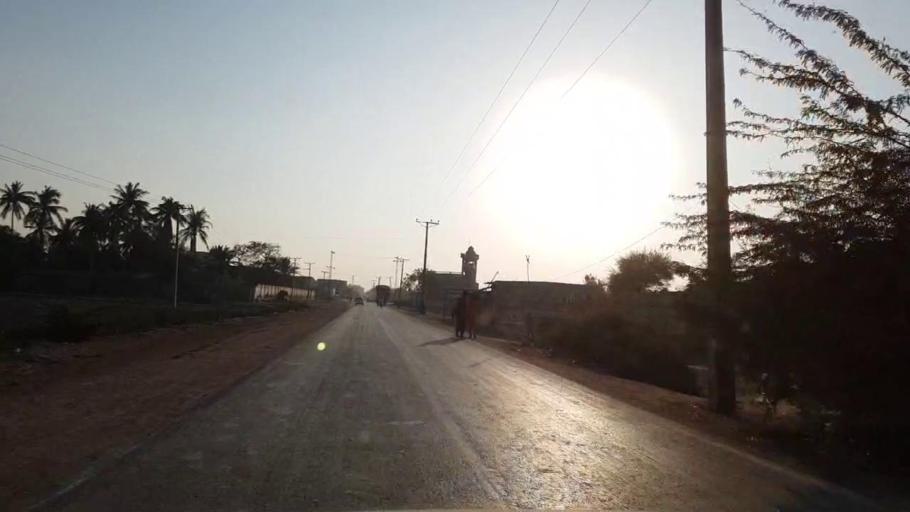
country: PK
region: Sindh
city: Daro Mehar
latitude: 24.6096
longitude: 68.0852
